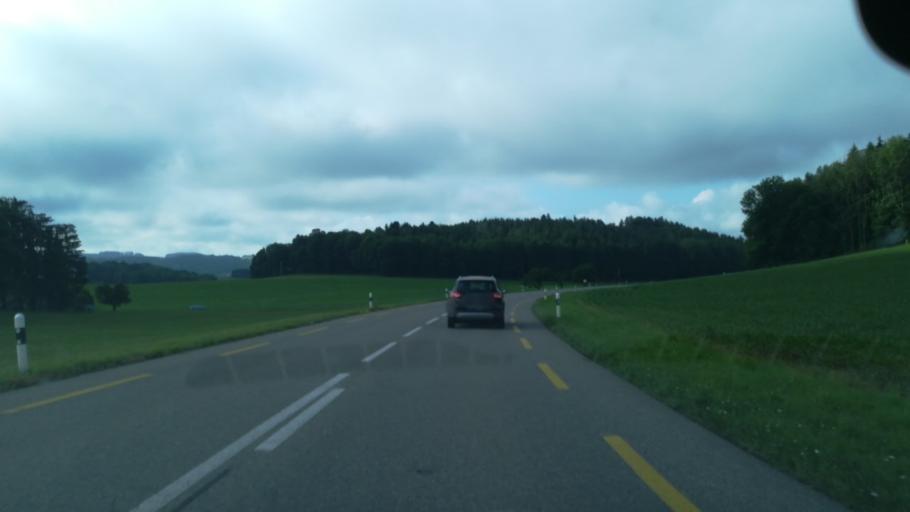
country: CH
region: Saint Gallen
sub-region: Wahlkreis St. Gallen
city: Waldkirch
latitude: 47.4926
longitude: 9.2586
